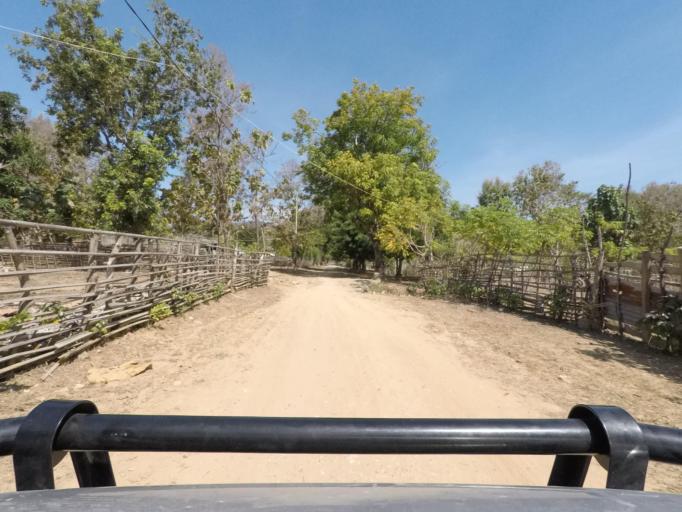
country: TL
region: Liquica
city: Maubara
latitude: -8.7850
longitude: 125.1034
